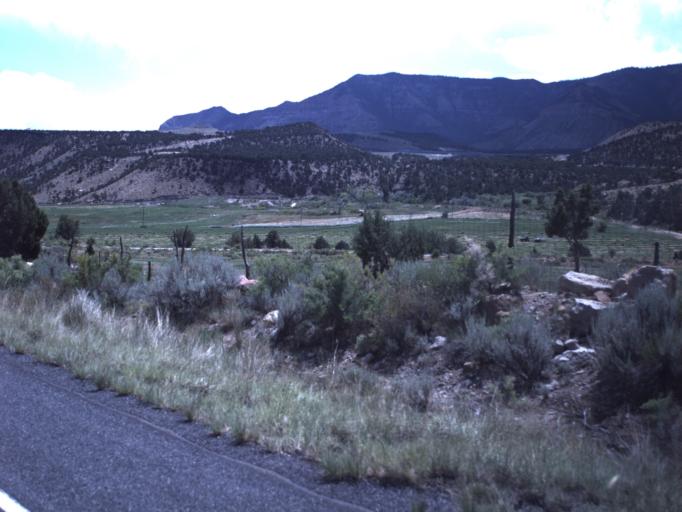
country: US
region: Utah
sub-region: Emery County
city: Huntington
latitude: 39.3807
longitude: -111.0726
